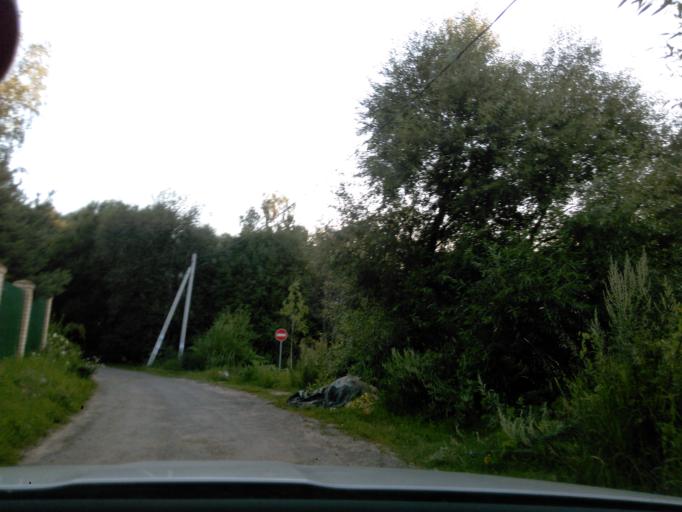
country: RU
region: Moskovskaya
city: Solnechnogorsk
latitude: 56.1277
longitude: 36.8366
